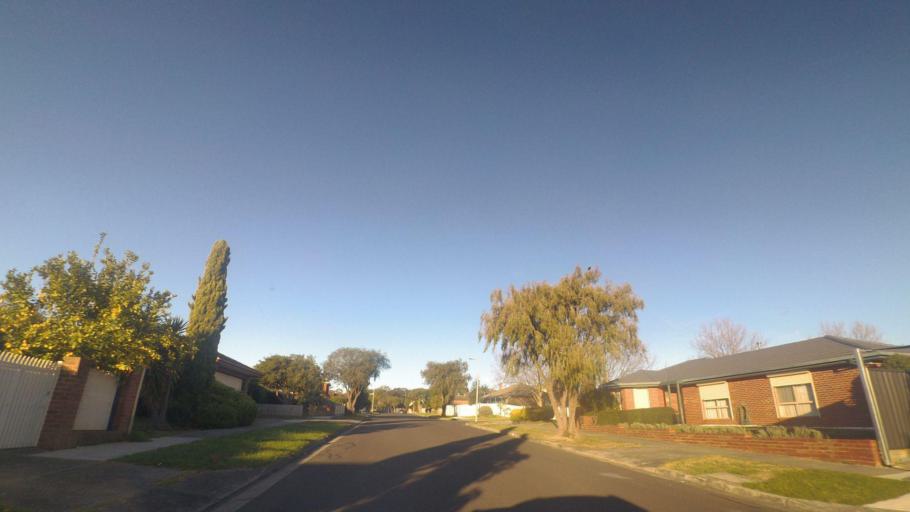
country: AU
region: Victoria
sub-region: Knox
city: Rowville
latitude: -37.9190
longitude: 145.2561
